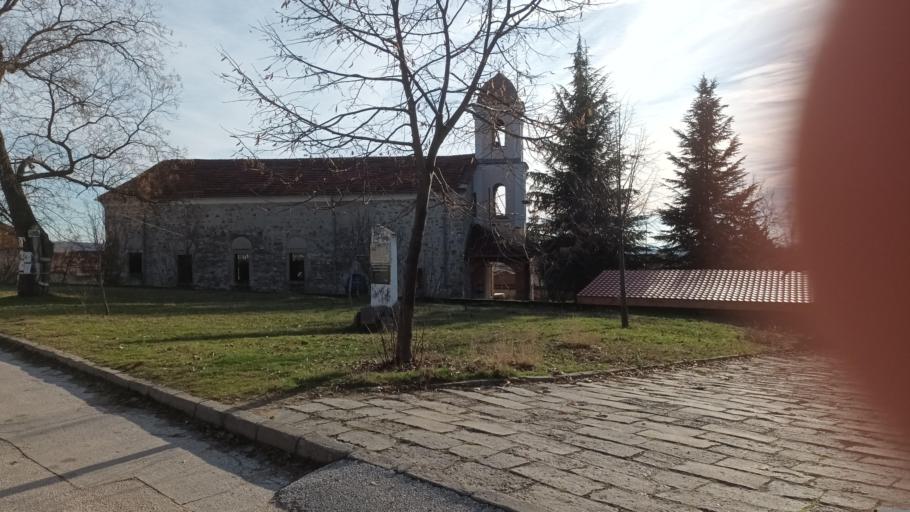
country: BG
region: Plovdiv
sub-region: Obshtina Khisarya
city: Khisarya
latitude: 42.5229
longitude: 24.7214
